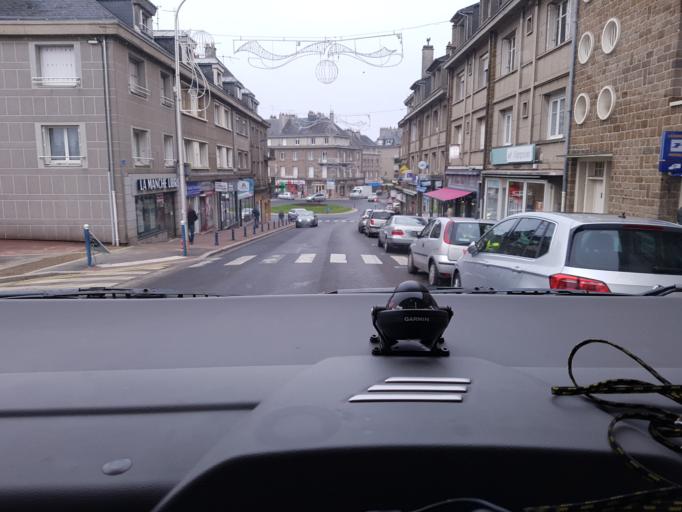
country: FR
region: Lower Normandy
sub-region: Departement du Calvados
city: Vire
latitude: 48.8381
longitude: -0.8883
